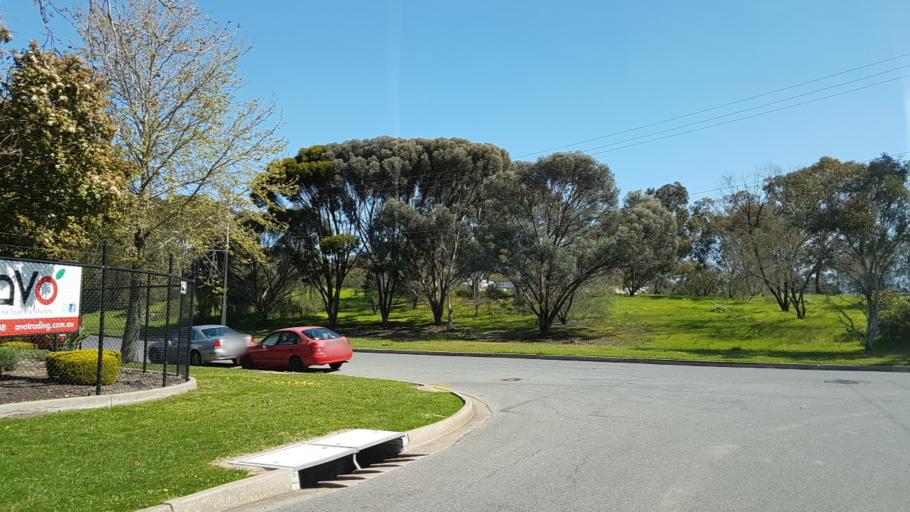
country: AU
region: South Australia
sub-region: Tea Tree Gully
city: Modbury
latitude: -34.8466
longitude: 138.6790
